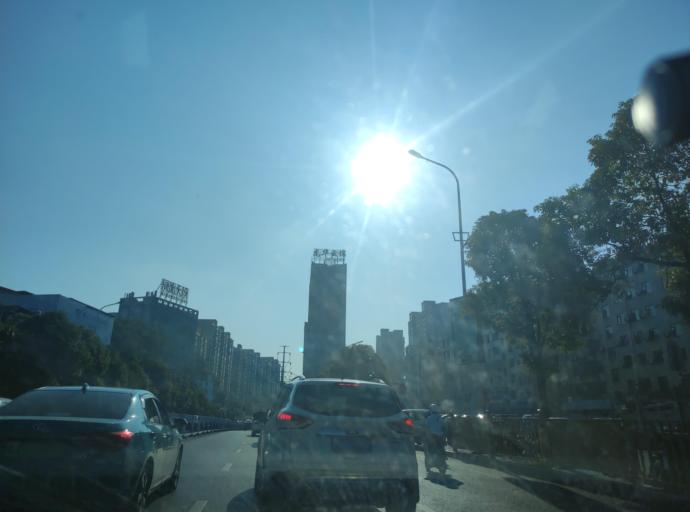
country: CN
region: Jiangxi Sheng
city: Pingxiang
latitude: 27.6336
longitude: 113.8614
